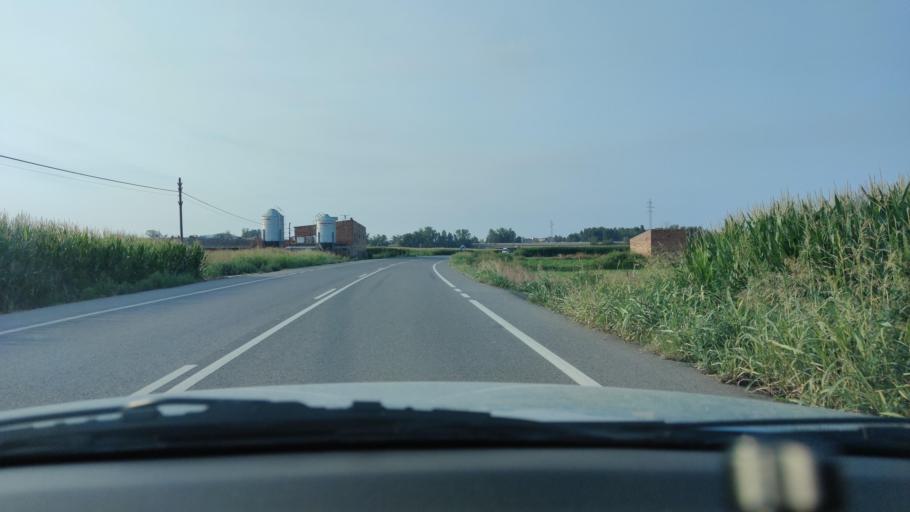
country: ES
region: Catalonia
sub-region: Provincia de Lleida
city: Torres de Segre
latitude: 41.5446
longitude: 0.5125
